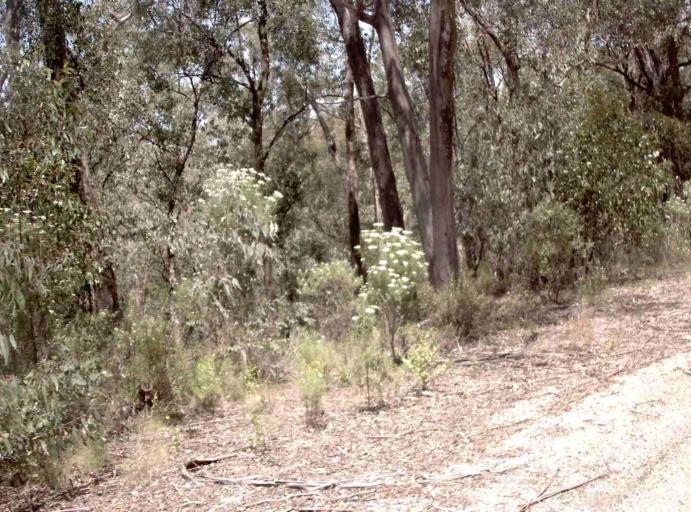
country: AU
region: Victoria
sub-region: East Gippsland
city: Lakes Entrance
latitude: -37.6073
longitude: 147.8826
